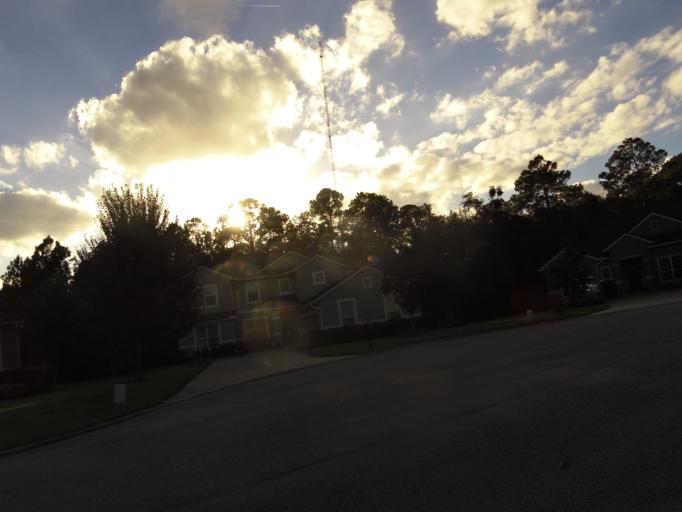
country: US
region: Florida
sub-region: Saint Johns County
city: Fruit Cove
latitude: 30.0695
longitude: -81.6448
